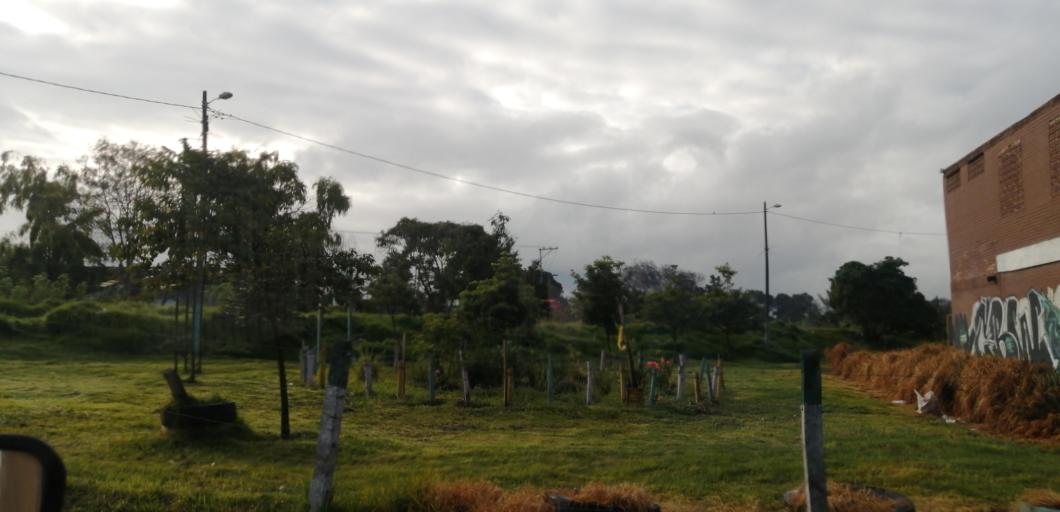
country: CO
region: Cundinamarca
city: Soacha
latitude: 4.5898
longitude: -74.1520
